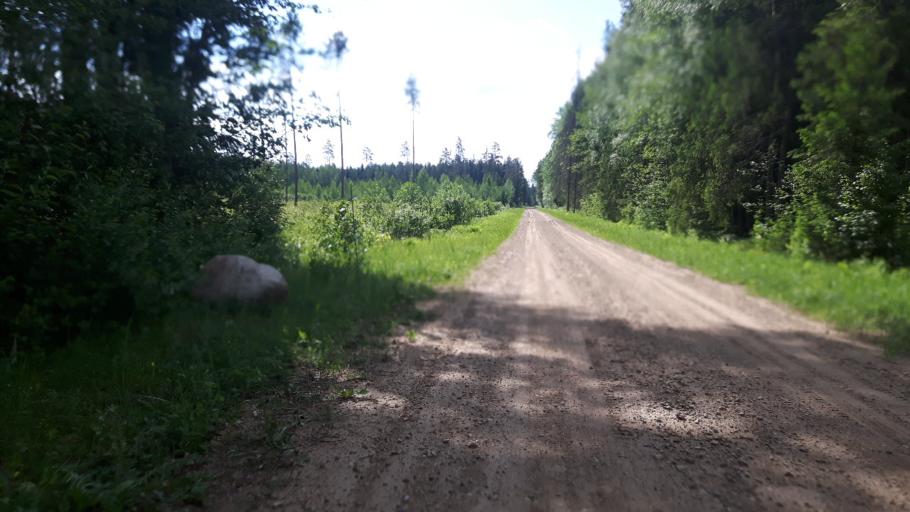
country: EE
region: Paernumaa
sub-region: Vaendra vald (alev)
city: Vandra
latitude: 58.7296
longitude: 25.0295
